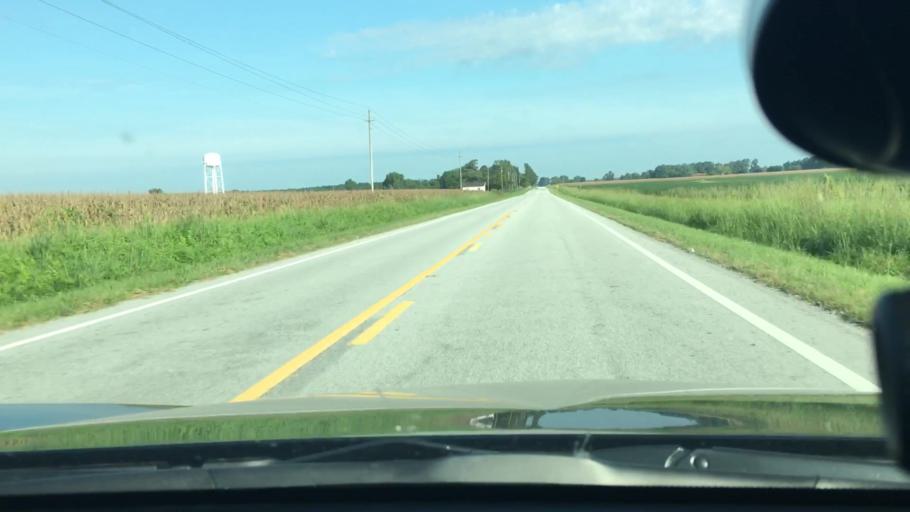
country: US
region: North Carolina
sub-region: Pitt County
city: Summerfield
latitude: 35.6513
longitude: -77.4648
